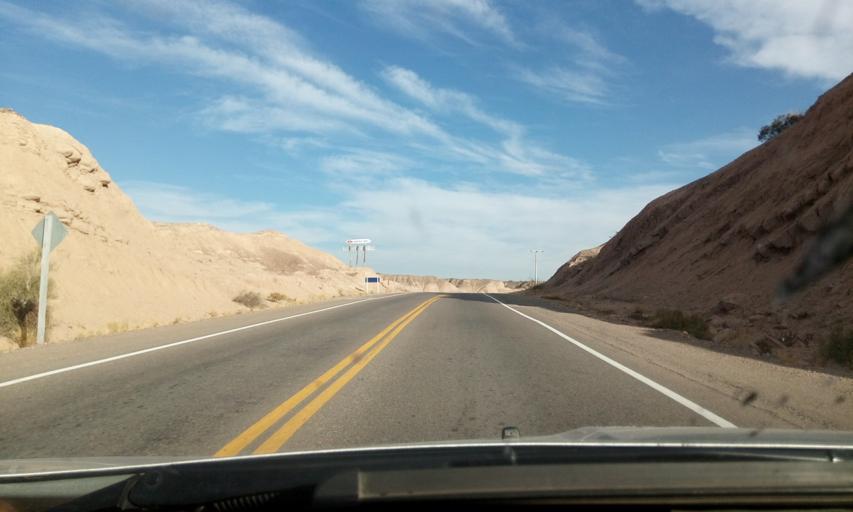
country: AR
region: San Juan
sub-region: Departamento de Rivadavia
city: Rivadavia
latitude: -31.4625
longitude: -68.6401
